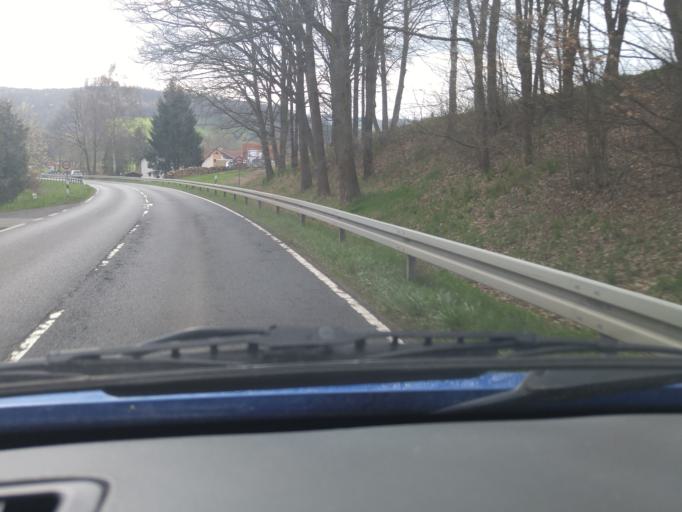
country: DE
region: Hesse
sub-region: Regierungsbezirk Kassel
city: Hosenfeld
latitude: 50.5440
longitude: 9.4931
